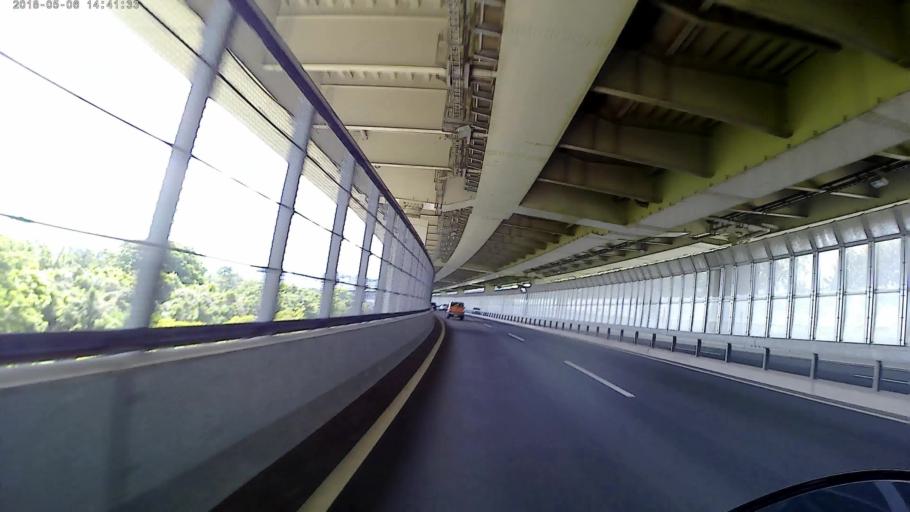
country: JP
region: Kanagawa
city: Yokohama
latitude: 35.4169
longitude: 139.6537
